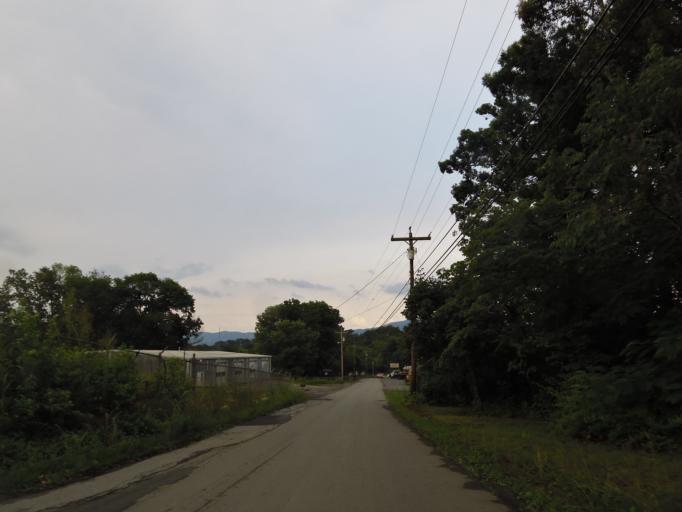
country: US
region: Tennessee
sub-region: Blount County
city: Wildwood
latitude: 35.8126
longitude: -83.8272
